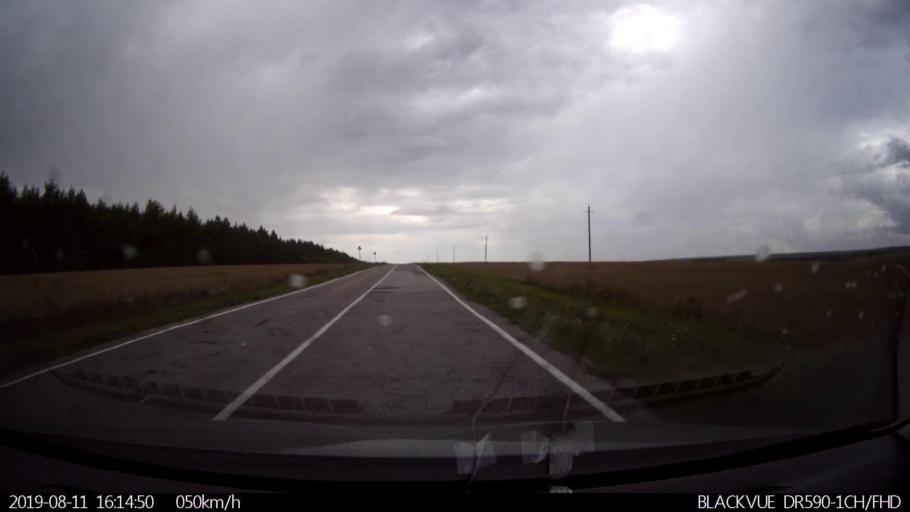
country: RU
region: Ulyanovsk
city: Mayna
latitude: 54.0309
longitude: 47.6319
